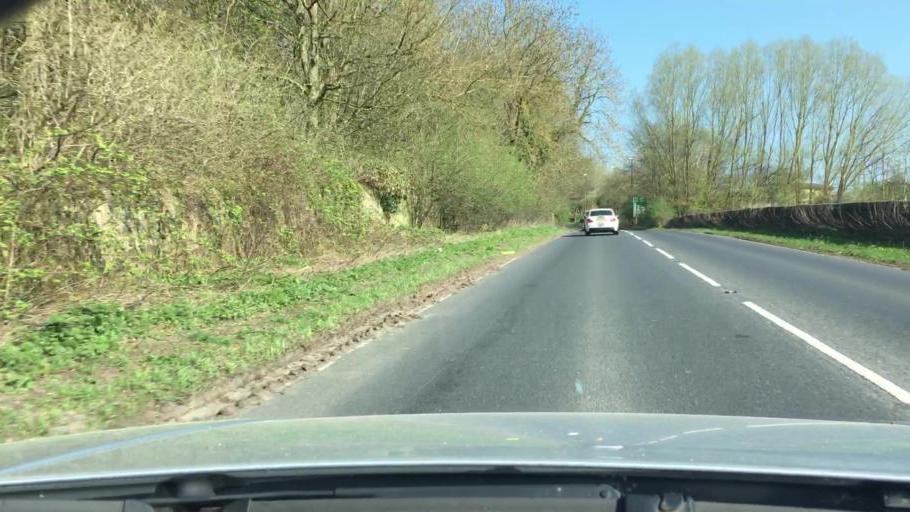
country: GB
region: England
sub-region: City and Borough of Leeds
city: Shadwell
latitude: 53.8957
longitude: -1.5102
